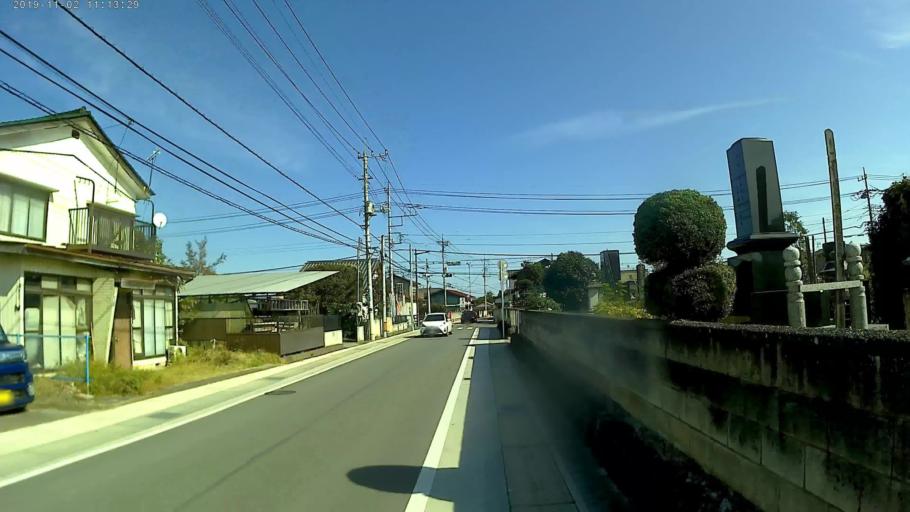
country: JP
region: Gunma
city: Annaka
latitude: 36.3108
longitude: 138.8464
